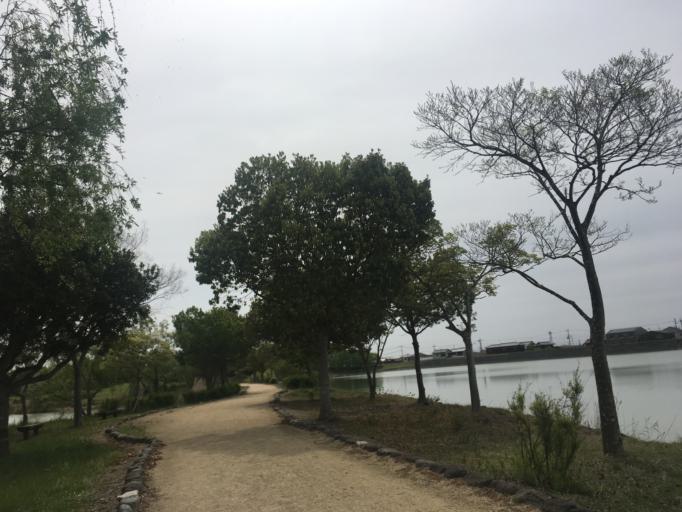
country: JP
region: Hyogo
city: Miki
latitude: 34.7637
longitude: 134.9243
